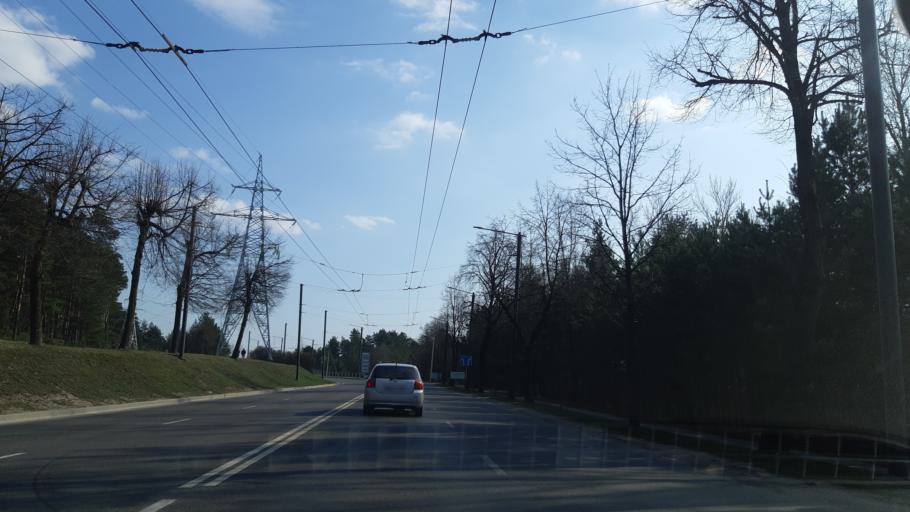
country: LT
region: Kauno apskritis
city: Dainava (Kaunas)
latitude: 54.8832
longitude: 24.0080
